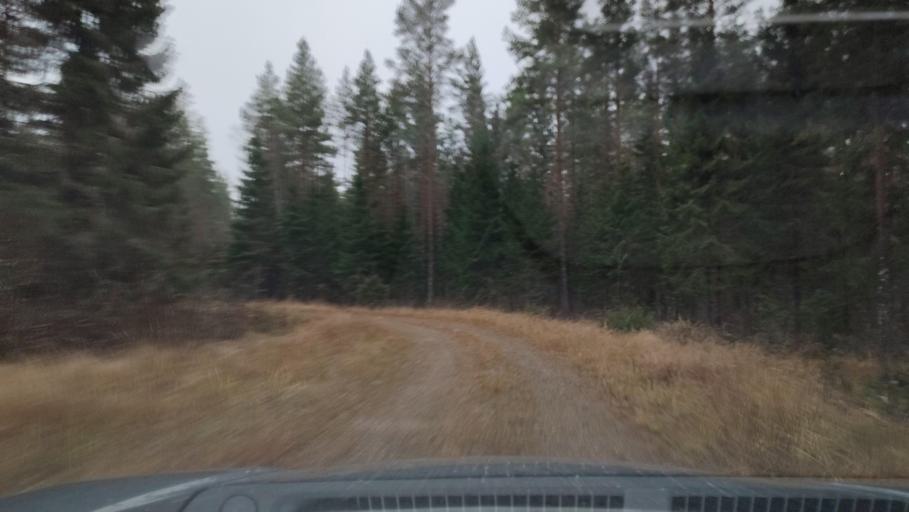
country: FI
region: Southern Ostrobothnia
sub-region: Suupohja
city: Karijoki
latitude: 62.1459
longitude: 21.5934
